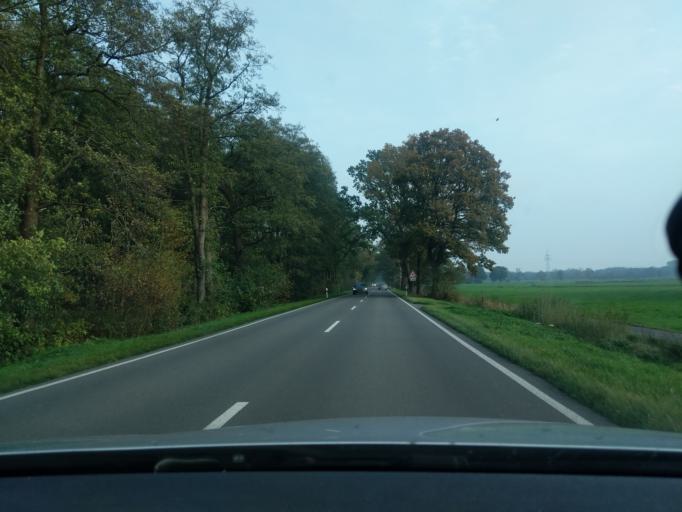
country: DE
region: Lower Saxony
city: Lamstedt
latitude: 53.6334
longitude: 9.1308
